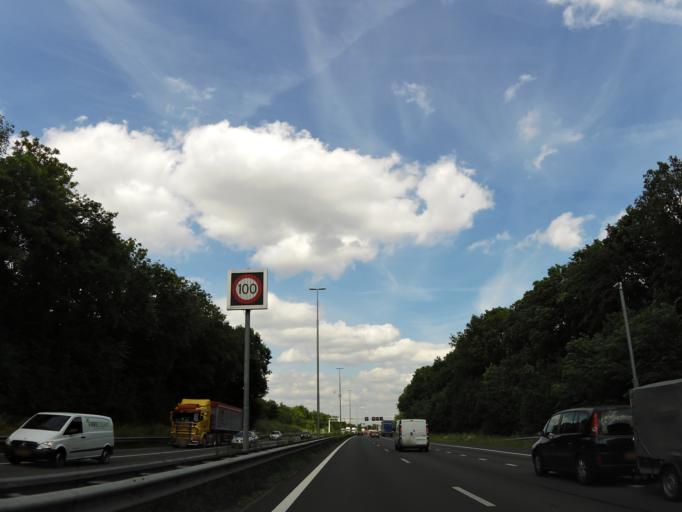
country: BE
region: Flanders
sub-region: Provincie Limburg
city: Maaseik
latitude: 51.0792
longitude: 5.8271
